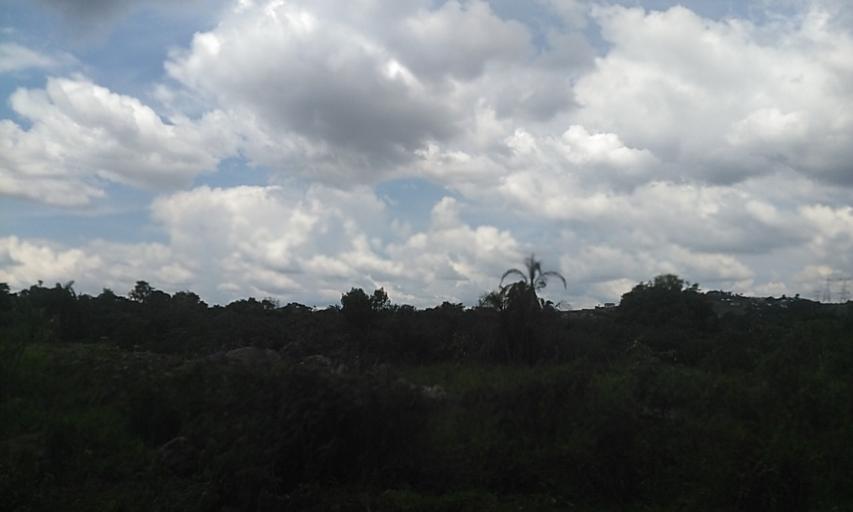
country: UG
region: Central Region
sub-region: Wakiso District
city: Wakiso
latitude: 0.3509
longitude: 32.4758
